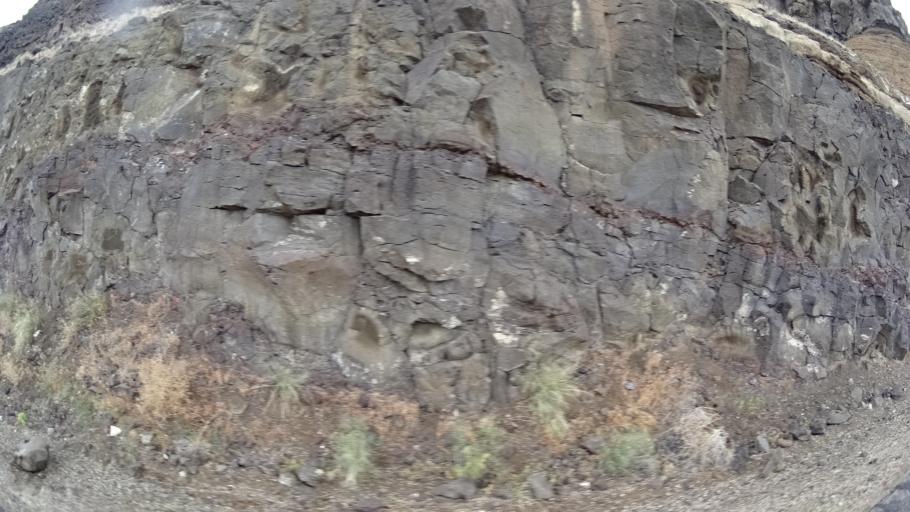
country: US
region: Idaho
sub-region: Owyhee County
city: Murphy
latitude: 43.2422
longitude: -116.3707
